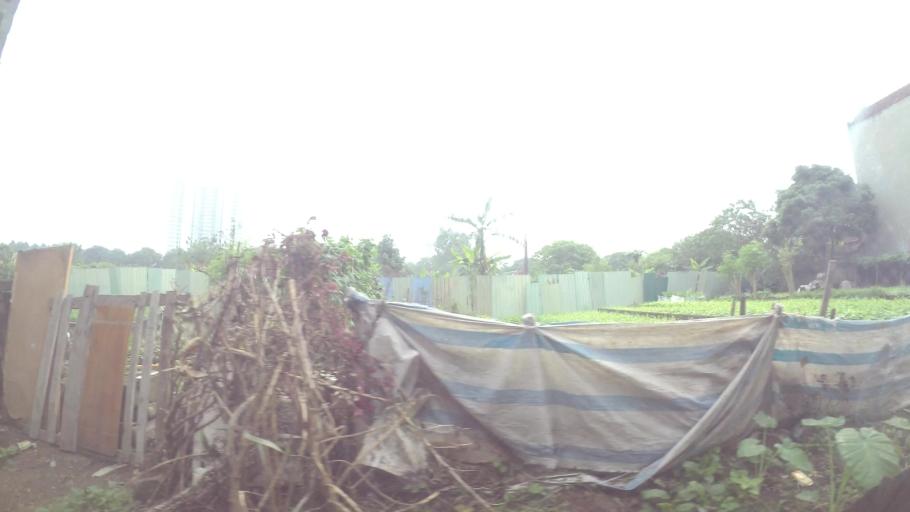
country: VN
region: Ha Noi
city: Van Dien
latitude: 20.9665
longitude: 105.8751
